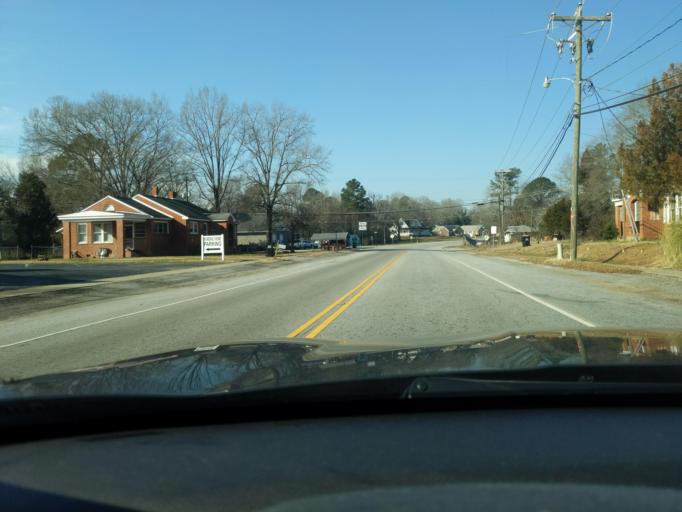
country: US
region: South Carolina
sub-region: Abbeville County
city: Calhoun Falls
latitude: 34.0902
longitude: -82.5867
